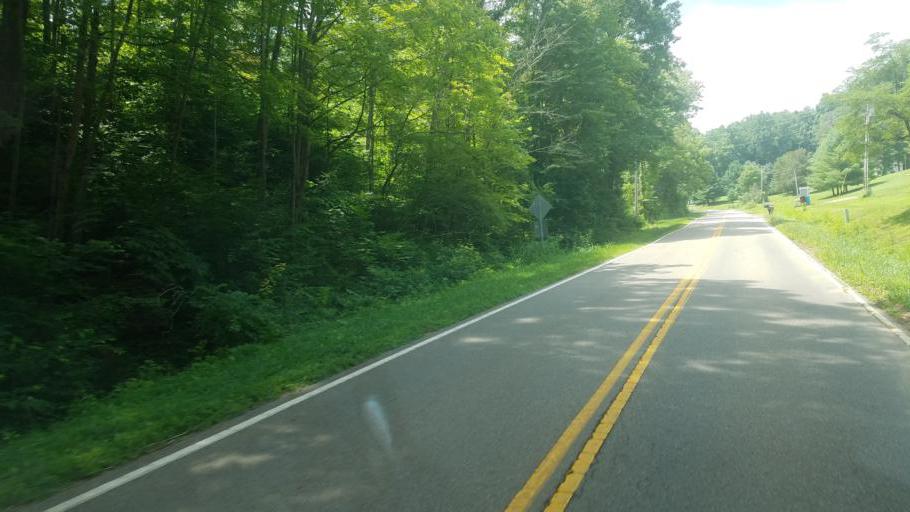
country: US
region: Ohio
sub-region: Ross County
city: Kingston
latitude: 39.4206
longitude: -82.7457
